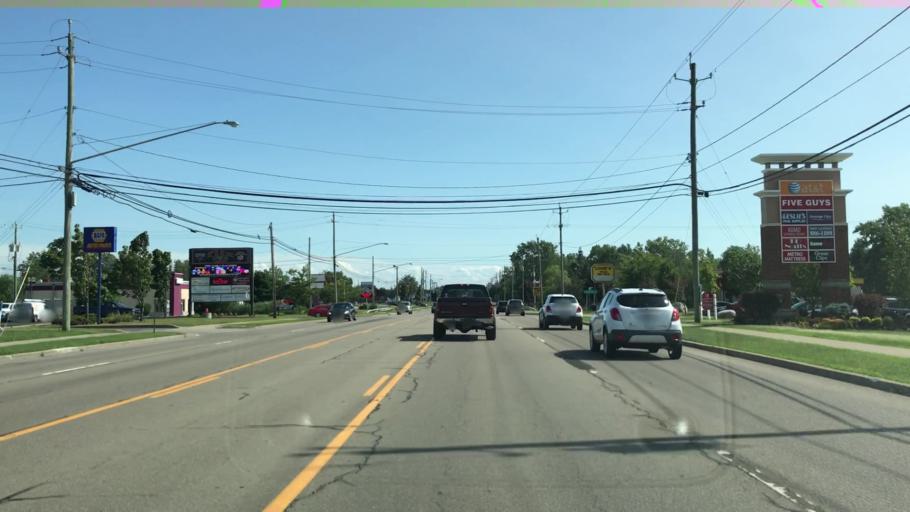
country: US
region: New York
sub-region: Erie County
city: Depew
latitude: 42.8778
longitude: -78.6970
